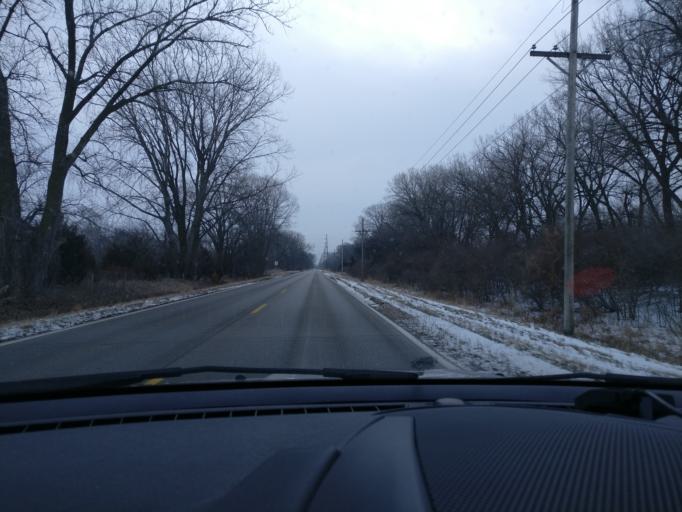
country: US
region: Nebraska
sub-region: Dodge County
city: Fremont
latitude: 41.4438
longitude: -96.5395
